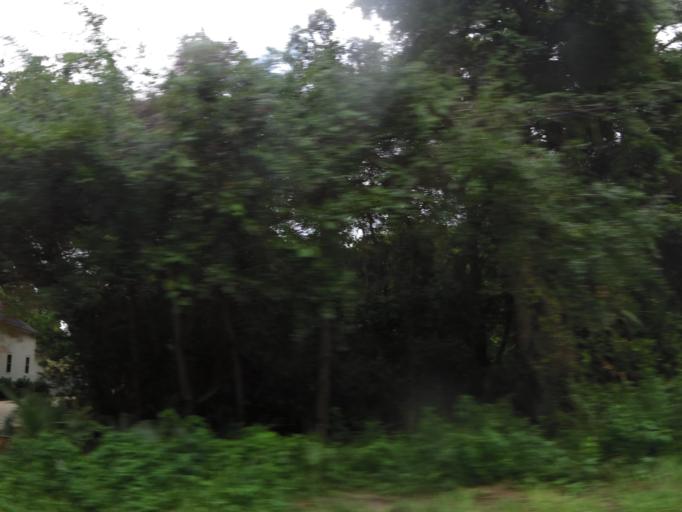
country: US
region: Georgia
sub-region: Glynn County
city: Saint Simons Island
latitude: 31.1420
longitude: -81.3848
